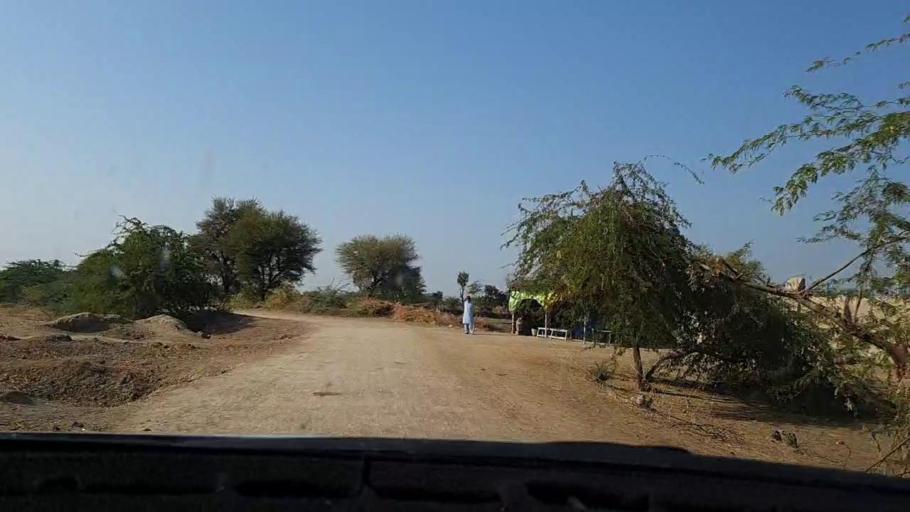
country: PK
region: Sindh
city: Tando Mittha Khan
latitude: 25.8151
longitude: 69.2886
